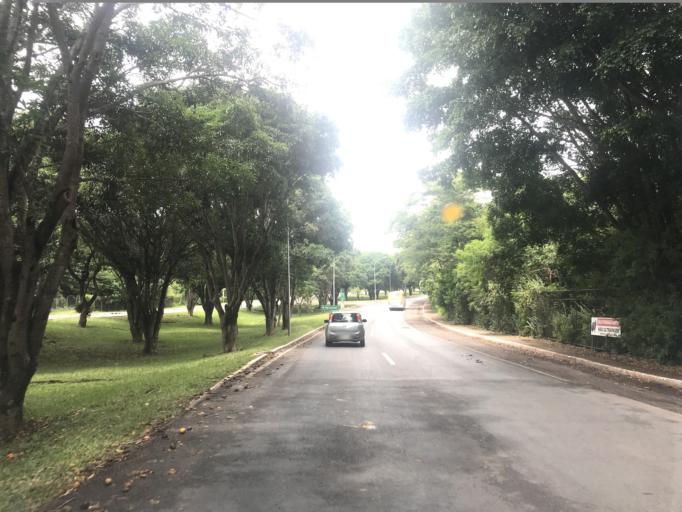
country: BR
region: Federal District
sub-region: Brasilia
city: Brasilia
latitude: -15.8403
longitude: -47.8391
